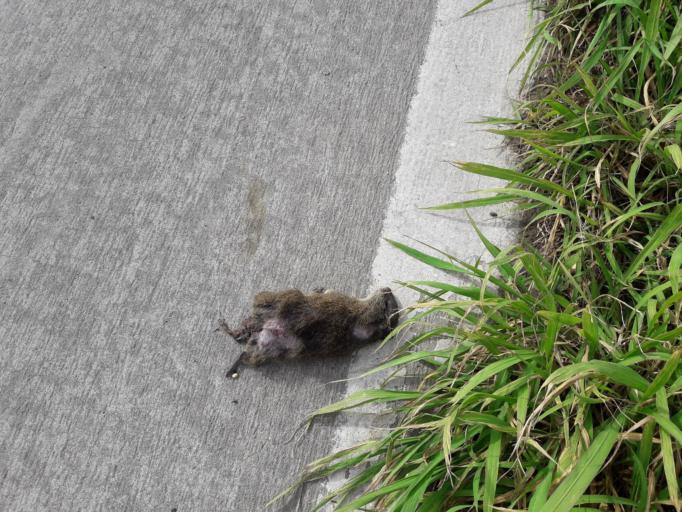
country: AR
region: Santa Fe
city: Santa Fe de la Vera Cruz
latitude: -31.6542
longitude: -60.6122
